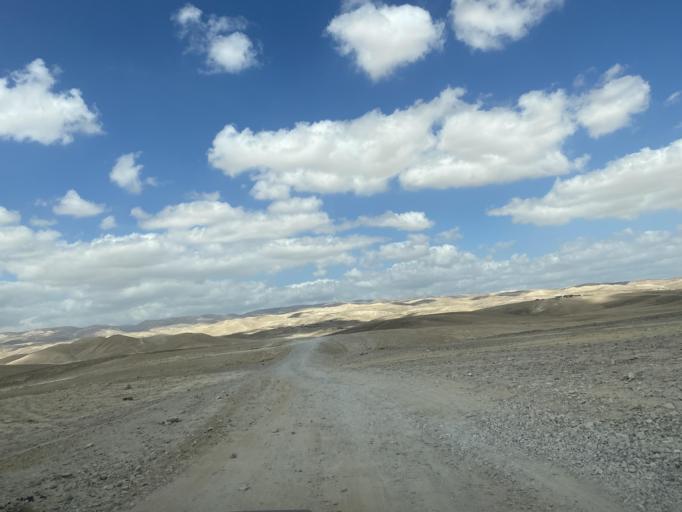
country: PS
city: `Arab ar Rashaydah
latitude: 31.5245
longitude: 35.2980
